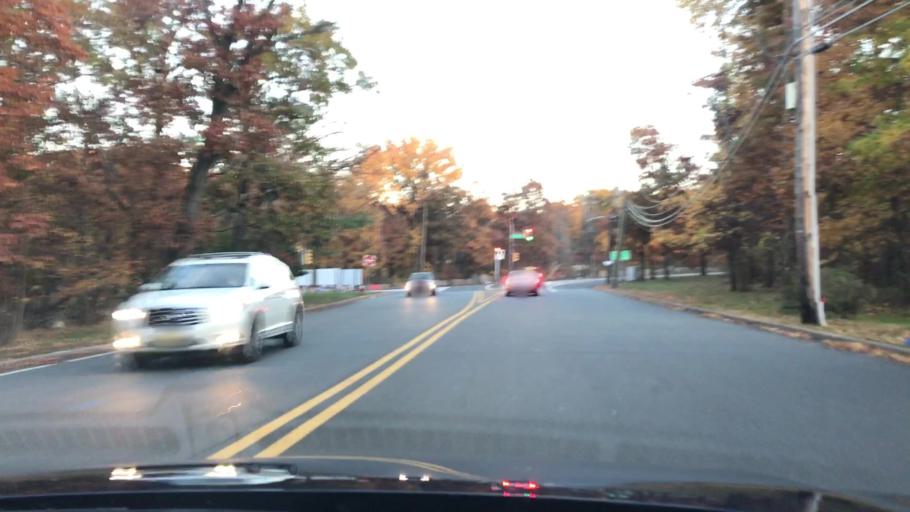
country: US
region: New Jersey
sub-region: Bergen County
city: Englewood Cliffs
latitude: 40.9035
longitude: -73.9381
